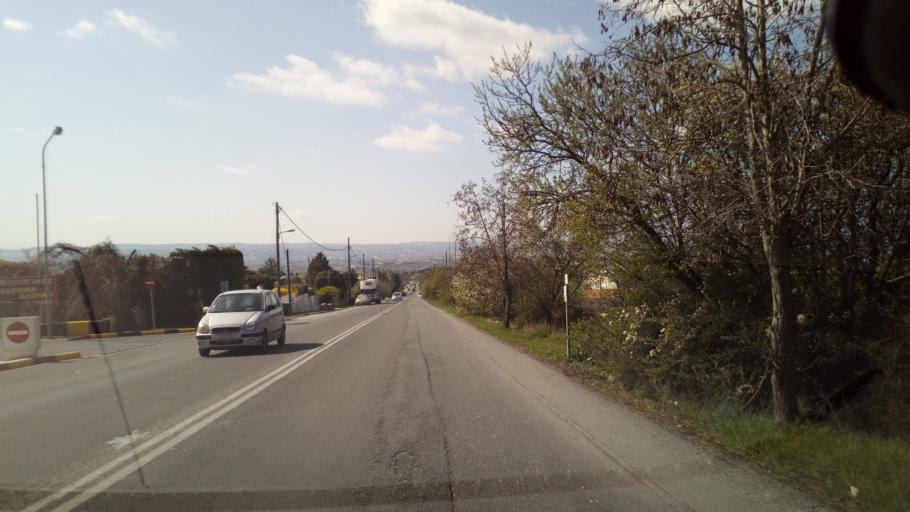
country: GR
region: Central Macedonia
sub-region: Nomos Thessalonikis
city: Thermi
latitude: 40.5624
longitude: 23.0239
